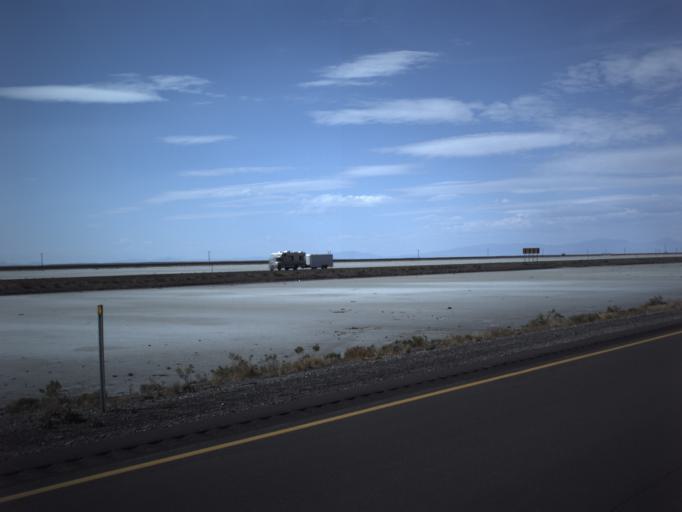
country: US
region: Utah
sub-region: Tooele County
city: Wendover
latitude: 40.7308
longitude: -113.4556
